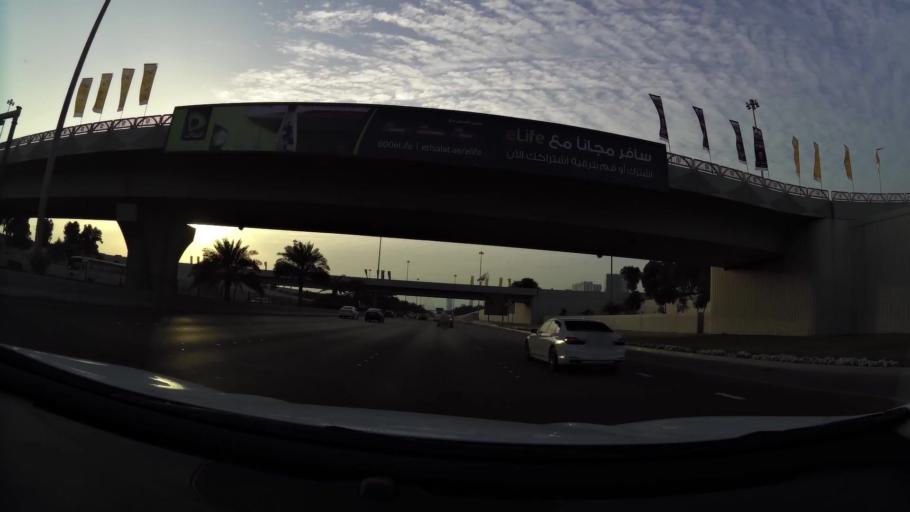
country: AE
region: Abu Dhabi
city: Abu Dhabi
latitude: 24.4076
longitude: 54.4720
